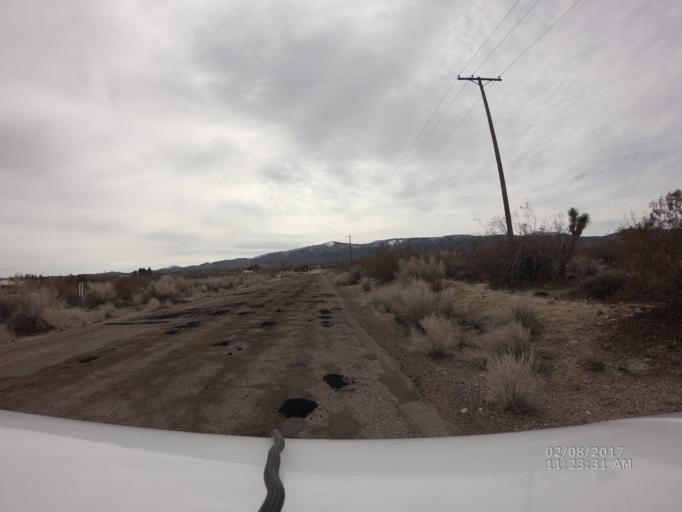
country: US
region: California
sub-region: San Bernardino County
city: Pinon Hills
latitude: 34.4571
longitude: -117.6598
